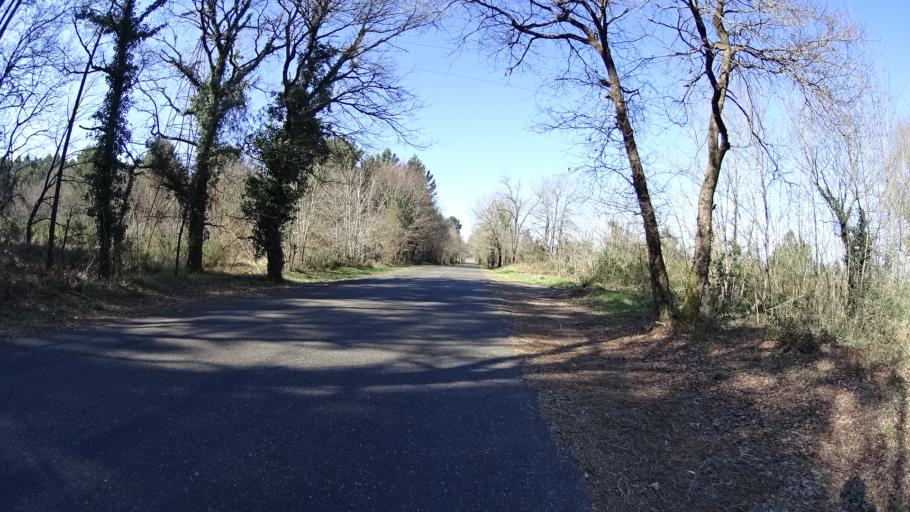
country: FR
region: Aquitaine
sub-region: Departement des Landes
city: Mees
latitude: 43.7325
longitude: -1.0942
